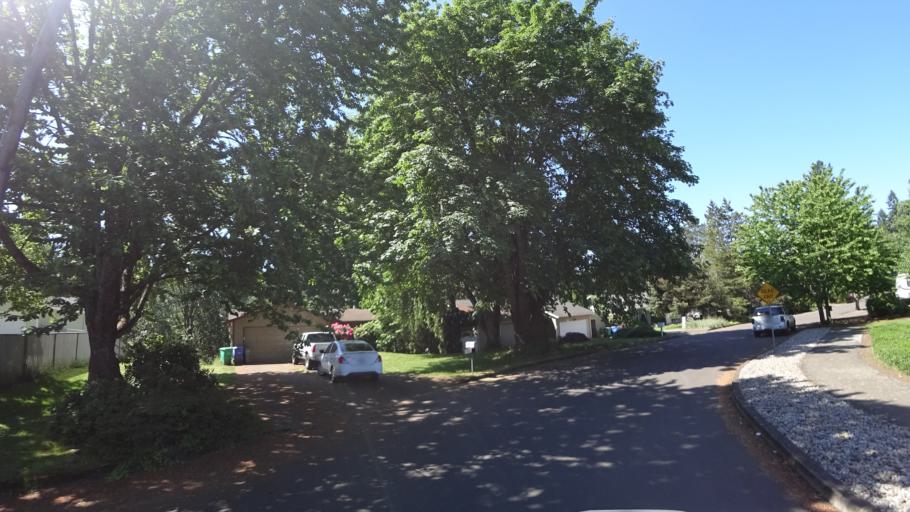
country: US
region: Oregon
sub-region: Clackamas County
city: Happy Valley
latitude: 45.4734
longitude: -122.5279
